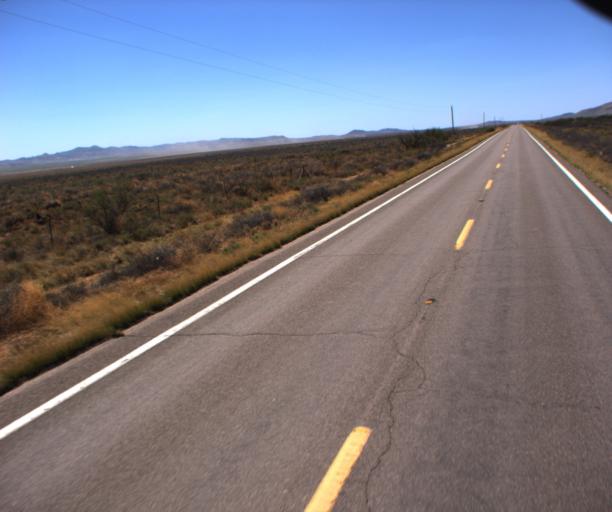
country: US
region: Arizona
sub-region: Cochise County
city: Douglas
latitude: 31.7619
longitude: -109.0832
